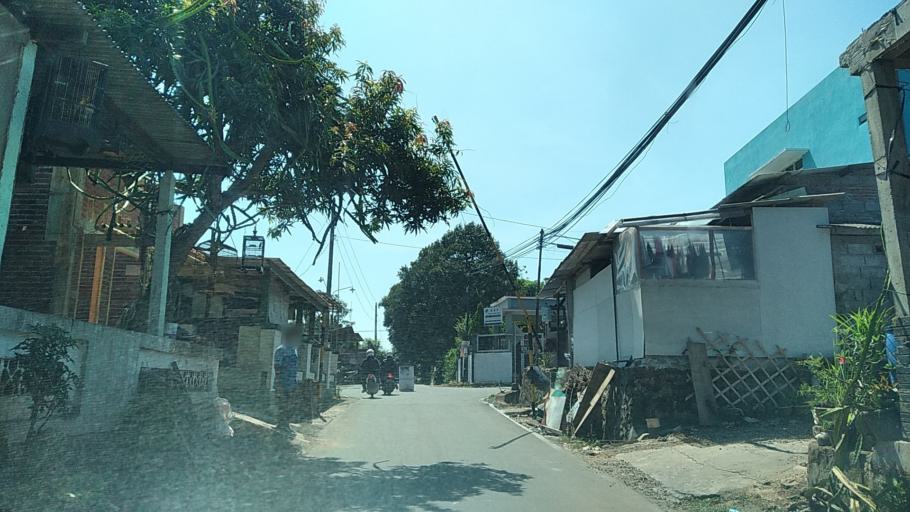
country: ID
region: Central Java
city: Ungaran
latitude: -7.1004
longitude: 110.4078
